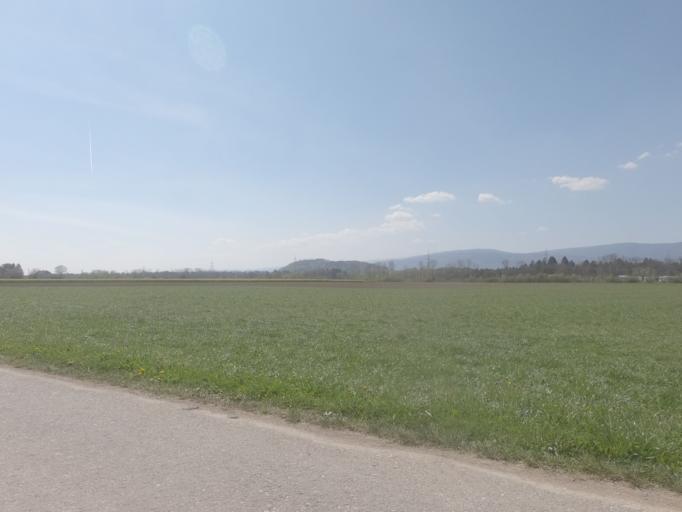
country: CH
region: Bern
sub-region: Biel/Bienne District
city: Orpund
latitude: 47.1131
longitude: 7.3367
